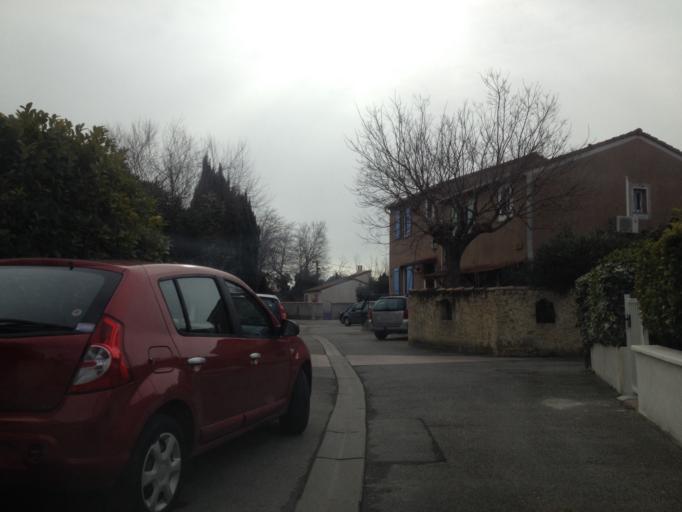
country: FR
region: Provence-Alpes-Cote d'Azur
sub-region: Departement du Vaucluse
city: Orange
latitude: 44.1397
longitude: 4.8207
